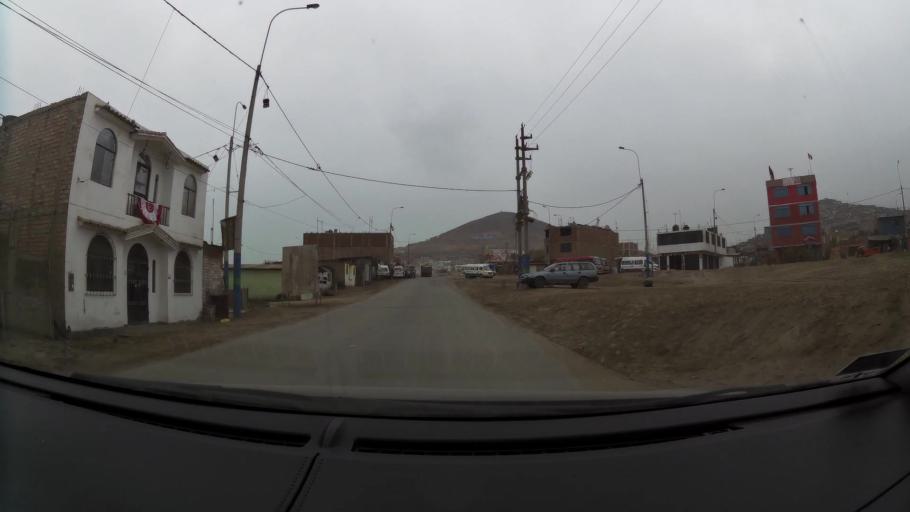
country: PE
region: Lima
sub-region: Lima
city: Santa Rosa
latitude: -11.8334
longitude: -77.1667
